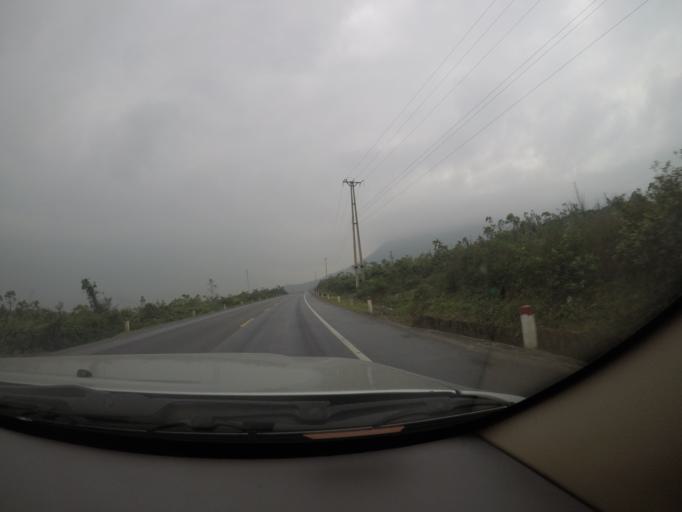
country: VN
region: Ha Tinh
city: Ky Anh
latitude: 18.0011
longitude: 106.4460
